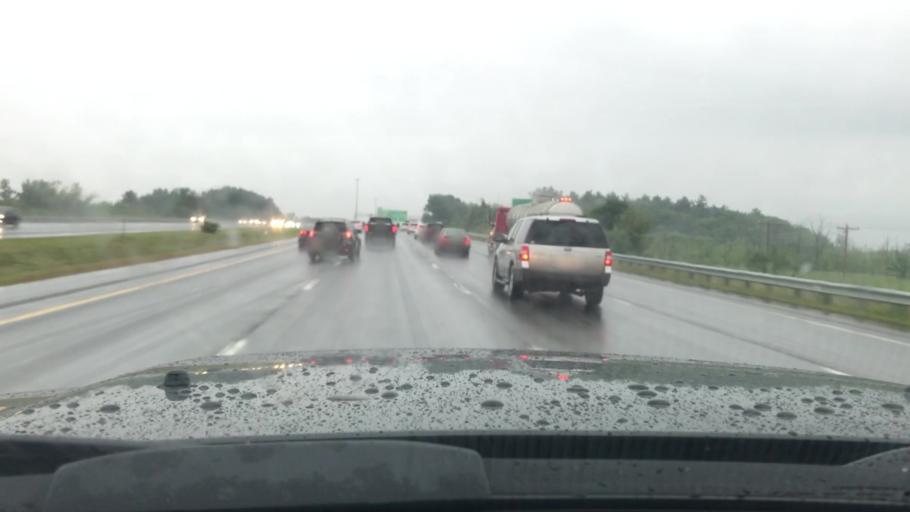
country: US
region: New Hampshire
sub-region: Rockingham County
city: Greenland
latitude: 43.0476
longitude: -70.8133
